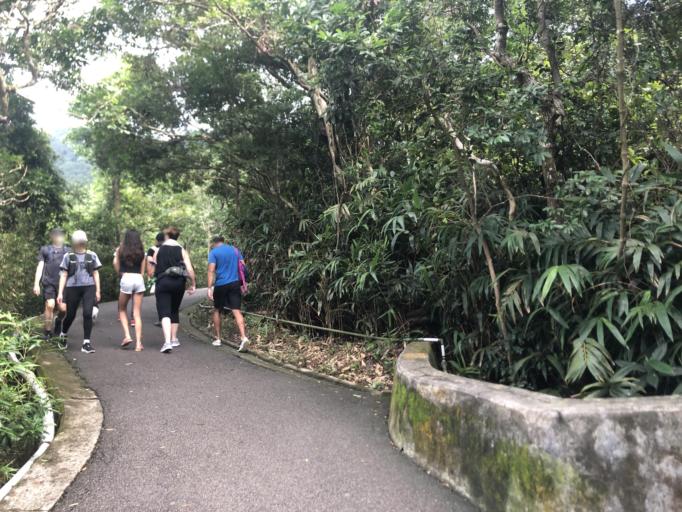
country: HK
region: Central and Western
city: Central
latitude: 22.2759
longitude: 114.1376
